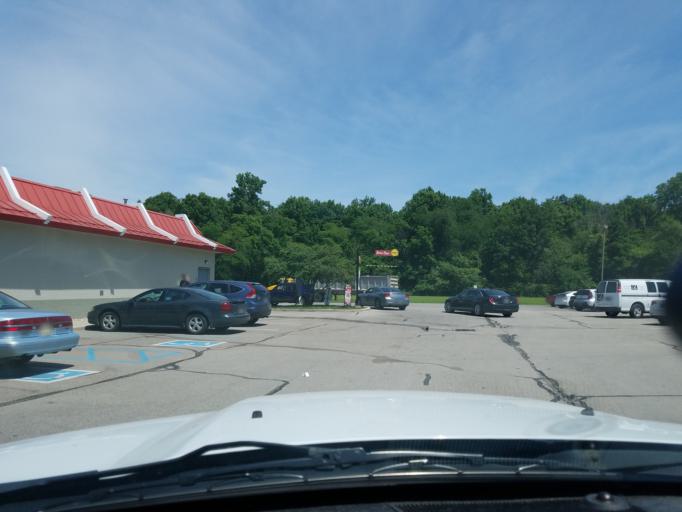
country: US
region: Indiana
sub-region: Delaware County
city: Albany
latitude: 40.3001
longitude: -85.2495
